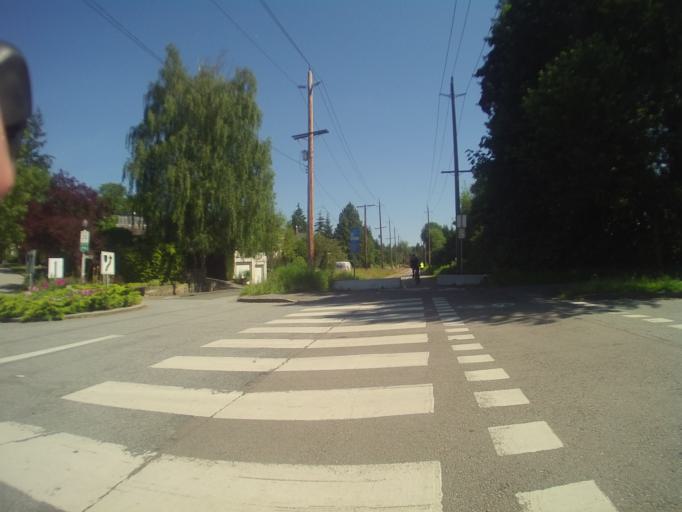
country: CA
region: British Columbia
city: Vancouver
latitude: 49.2475
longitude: -123.1502
